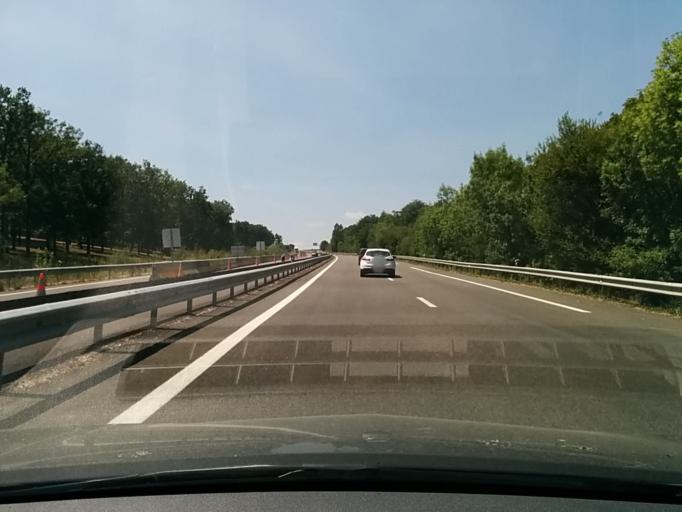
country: FR
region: Midi-Pyrenees
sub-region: Departement du Gers
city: Pujaudran
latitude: 43.5854
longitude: 1.1516
